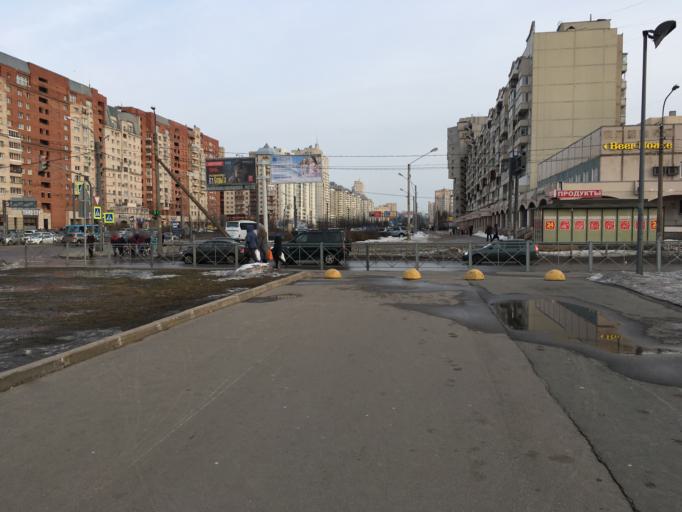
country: RU
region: St.-Petersburg
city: Staraya Derevnya
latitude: 60.0166
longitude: 30.2482
